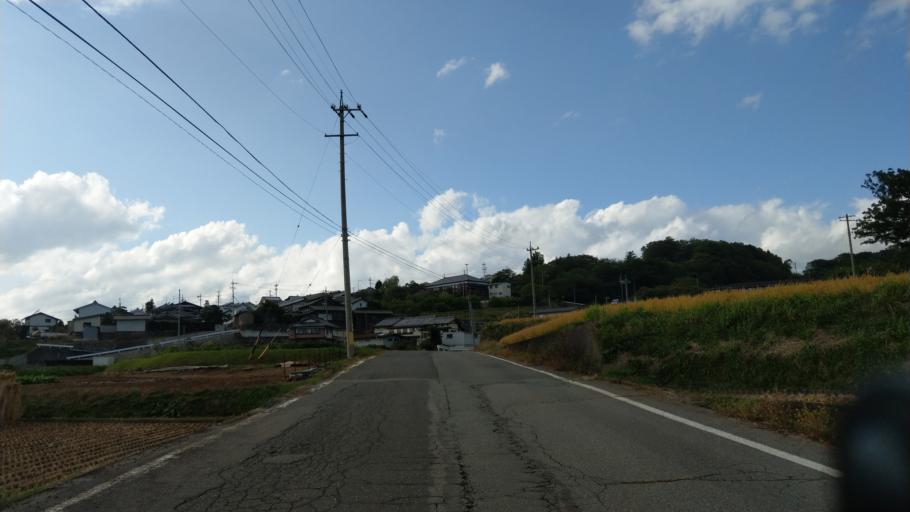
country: JP
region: Nagano
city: Komoro
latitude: 36.3480
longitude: 138.4134
